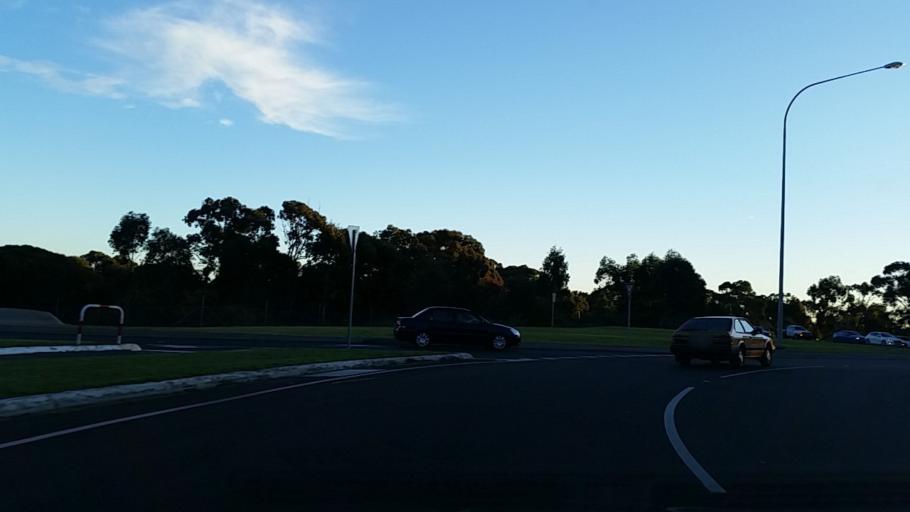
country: AU
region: South Australia
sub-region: Onkaparinga
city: Bedford Park
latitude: -35.0515
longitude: 138.5736
